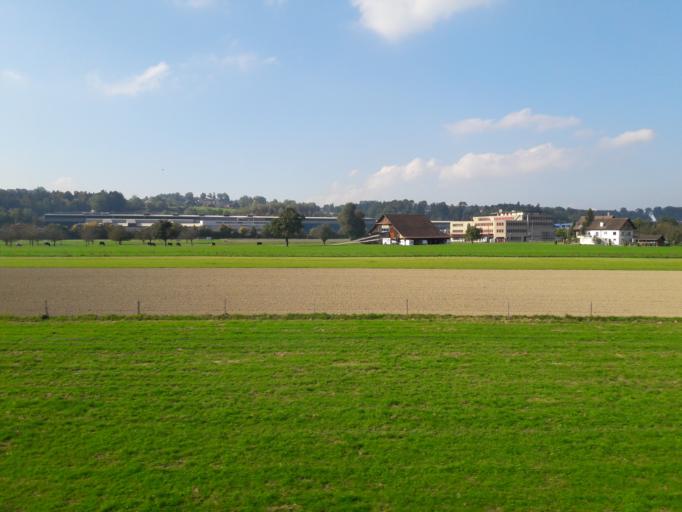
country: CH
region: Lucerne
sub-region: Lucerne-Stadt District
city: Littau
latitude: 47.0586
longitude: 8.2663
